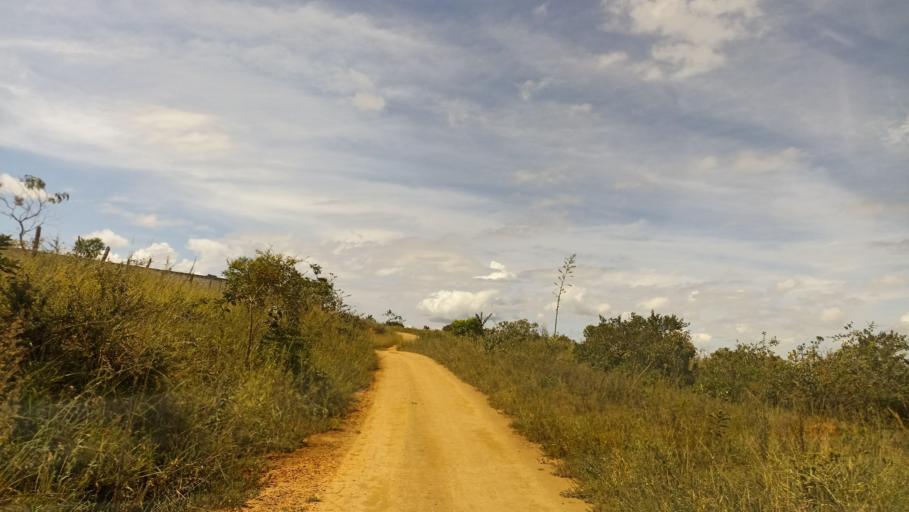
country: BR
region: Minas Gerais
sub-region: Itabirito
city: Itabirito
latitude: -20.3505
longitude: -43.7237
